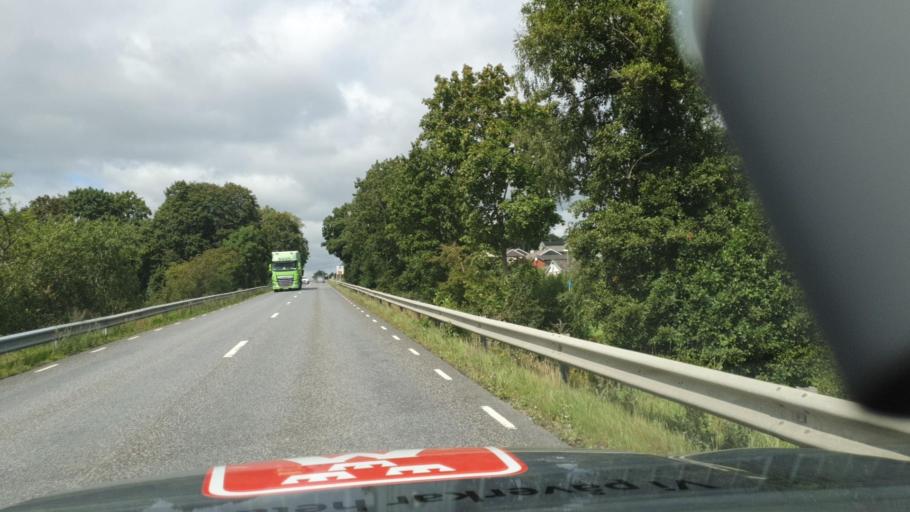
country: SE
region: Blekinge
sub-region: Karlskrona Kommun
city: Rodeby
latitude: 56.2578
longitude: 15.6113
